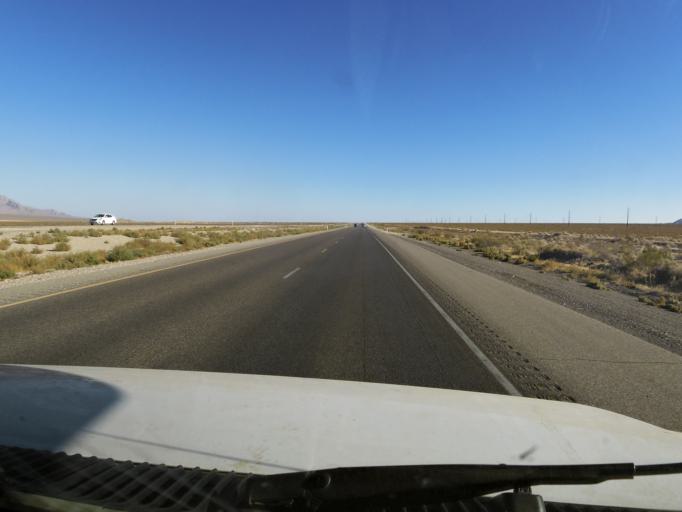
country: US
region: Nevada
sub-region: Clark County
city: Summerlin South
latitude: 36.4020
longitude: -115.4001
